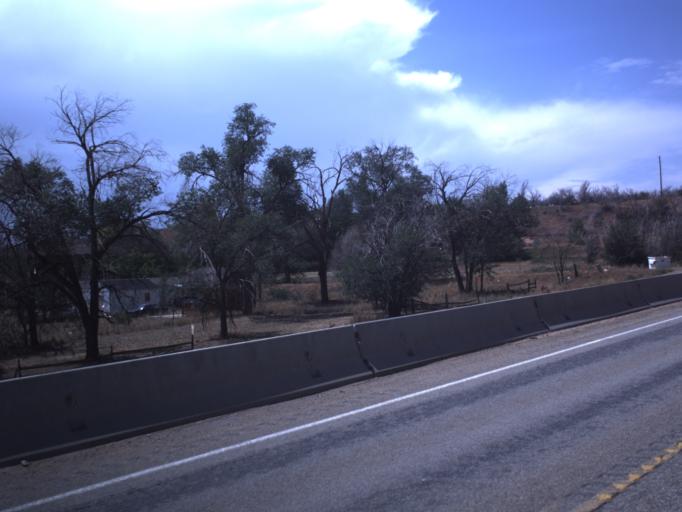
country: US
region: Utah
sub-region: Duchesne County
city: Roosevelt
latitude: 40.3020
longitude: -109.9127
